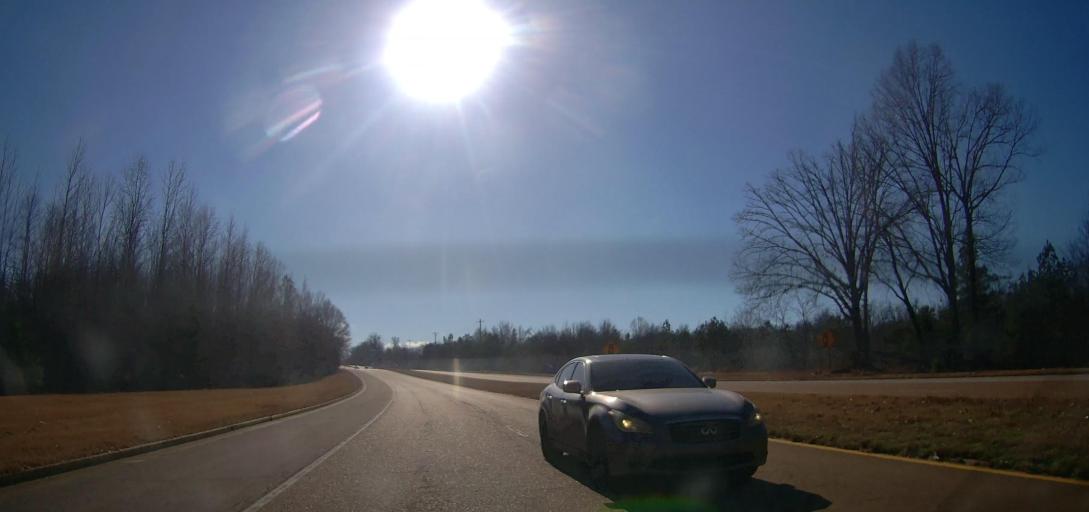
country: US
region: Tennessee
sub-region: Shelby County
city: Bartlett
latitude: 35.2458
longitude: -89.8967
